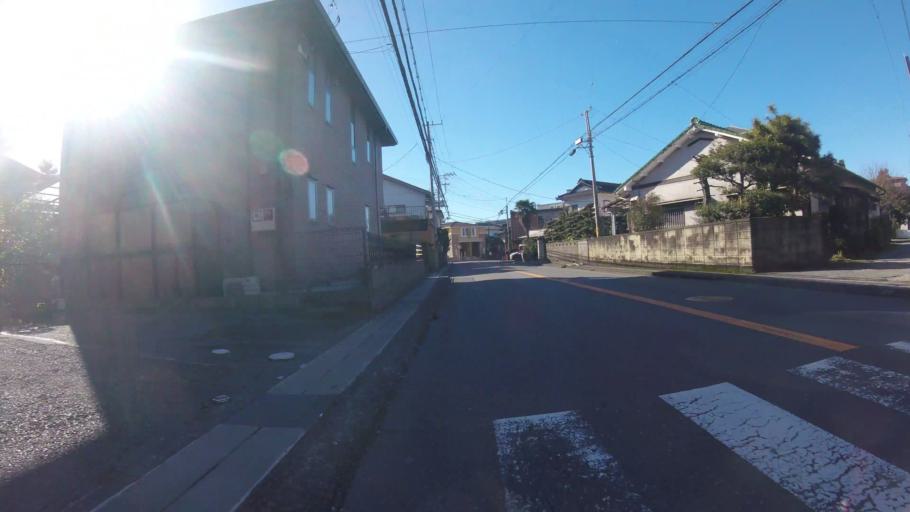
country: JP
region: Shizuoka
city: Mishima
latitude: 35.1080
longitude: 138.8957
